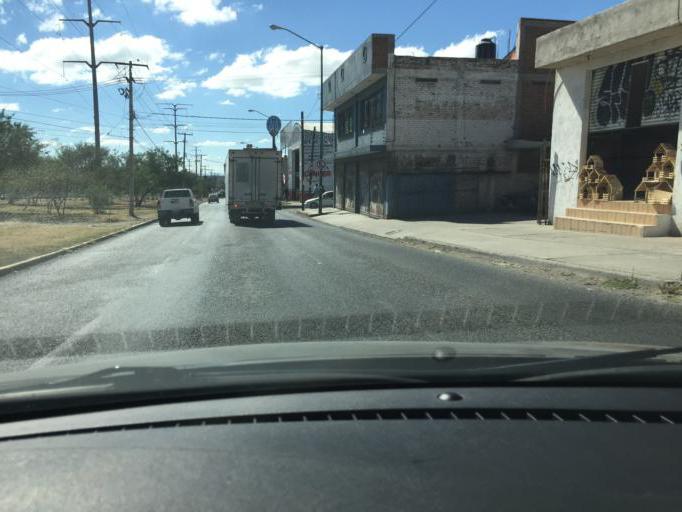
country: MX
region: Guanajuato
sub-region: Leon
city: Ejido la Joya
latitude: 21.1056
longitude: -101.7119
